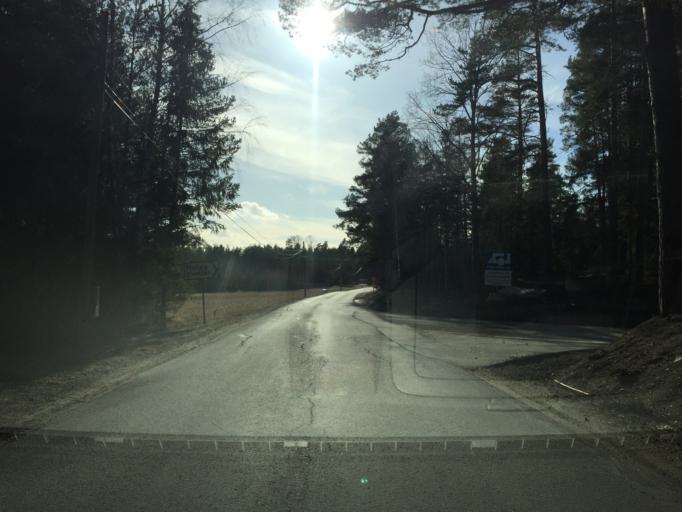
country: SE
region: Stockholm
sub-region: Nynashamns Kommun
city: Osmo
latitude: 59.0534
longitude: 17.8640
